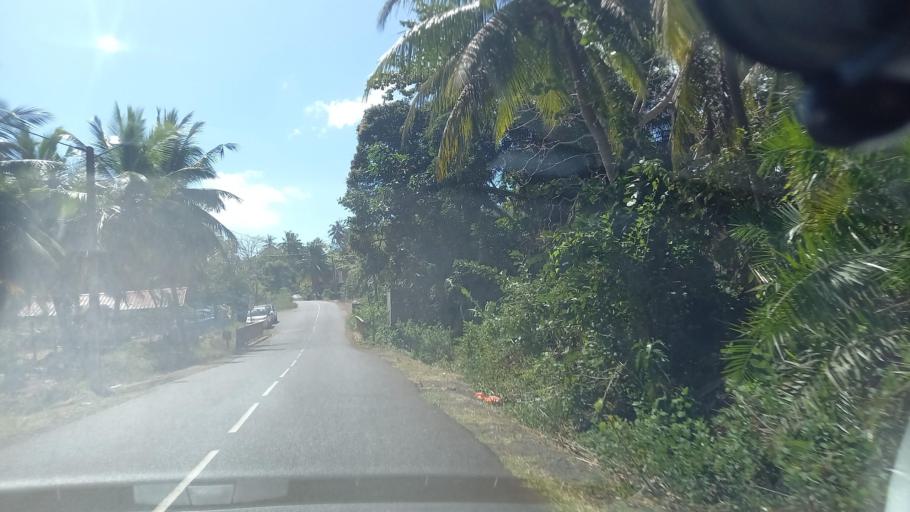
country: YT
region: Kani-Keli
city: Kani Keli
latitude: -12.9402
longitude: 45.1022
